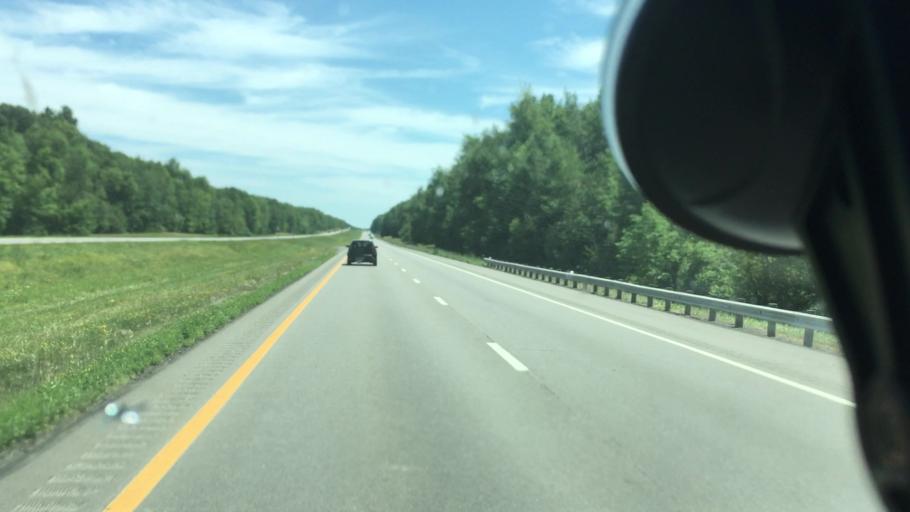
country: US
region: Ohio
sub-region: Mahoning County
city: Canfield
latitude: 41.0625
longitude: -80.7507
